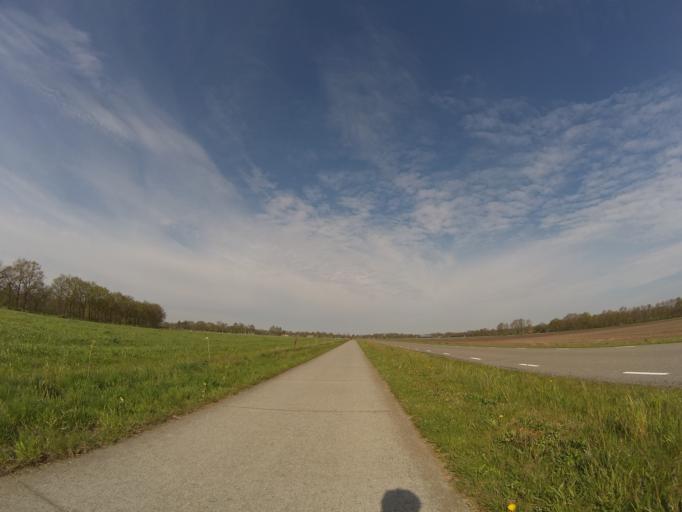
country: NL
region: Drenthe
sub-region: Gemeente Coevorden
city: Sleen
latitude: 52.7943
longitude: 6.7487
